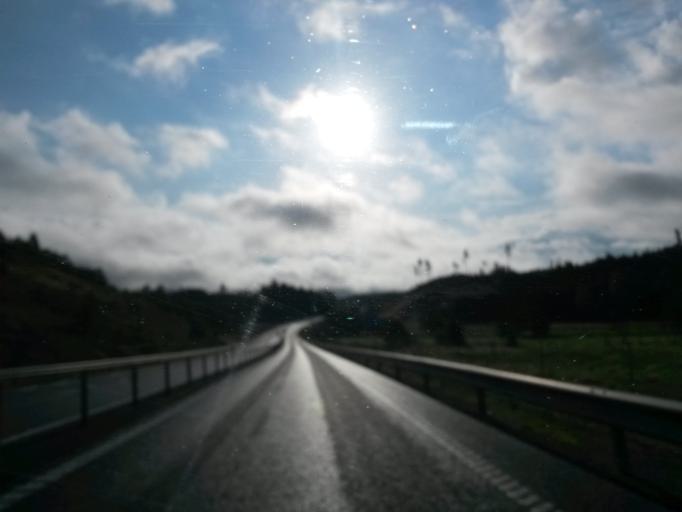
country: SE
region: Vaestra Goetaland
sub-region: Boras Kommun
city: Ganghester
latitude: 57.6712
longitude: 13.0150
